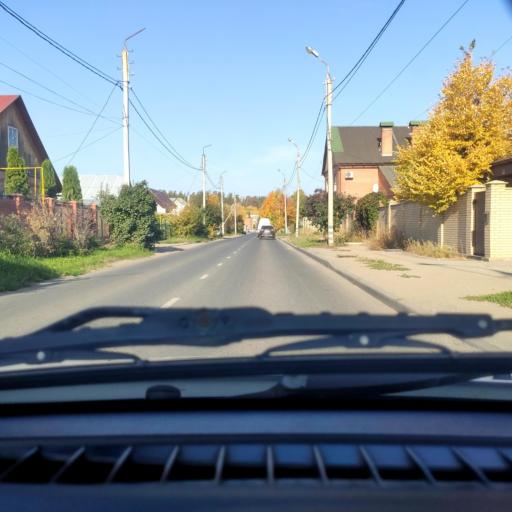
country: RU
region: Samara
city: Tol'yatti
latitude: 53.5087
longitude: 49.3971
